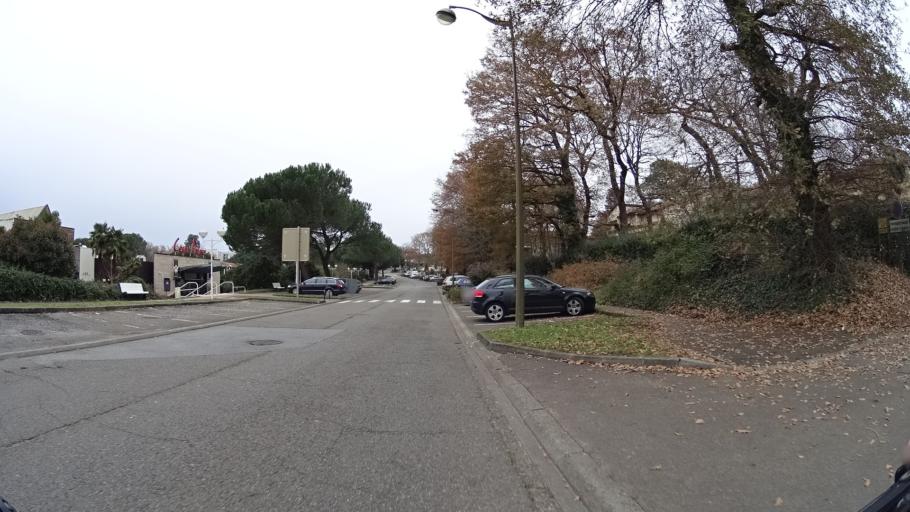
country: FR
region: Aquitaine
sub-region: Departement des Landes
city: Saint-Paul-les-Dax
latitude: 43.7257
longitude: -1.0638
